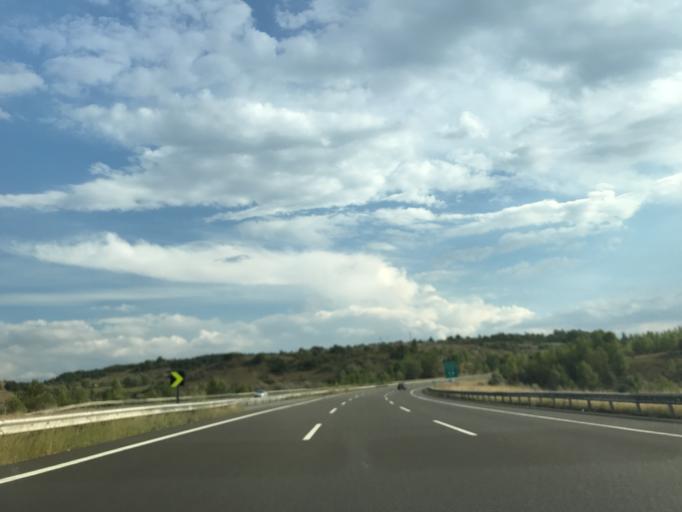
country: TR
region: Bolu
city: Gerede
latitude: 40.6550
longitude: 32.2369
